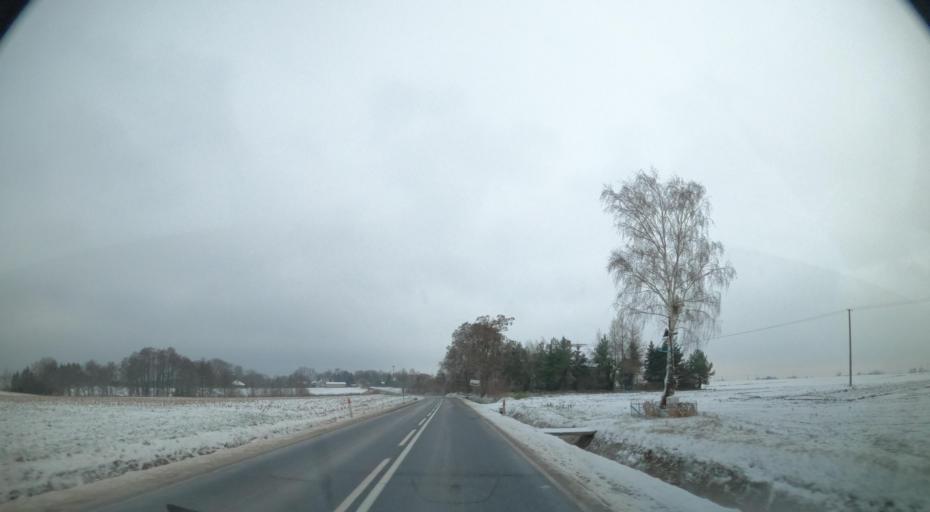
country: PL
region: Masovian Voivodeship
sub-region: Powiat plocki
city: Nowy Duninow
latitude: 52.6126
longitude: 19.4670
